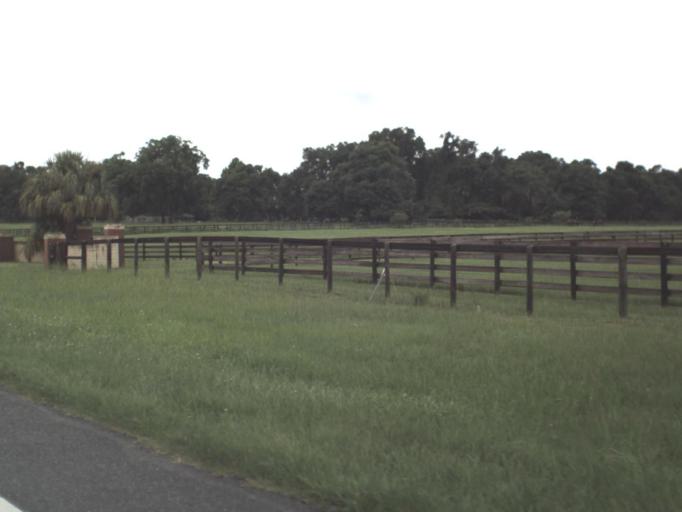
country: US
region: Florida
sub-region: Levy County
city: Williston
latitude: 29.3298
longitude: -82.4547
